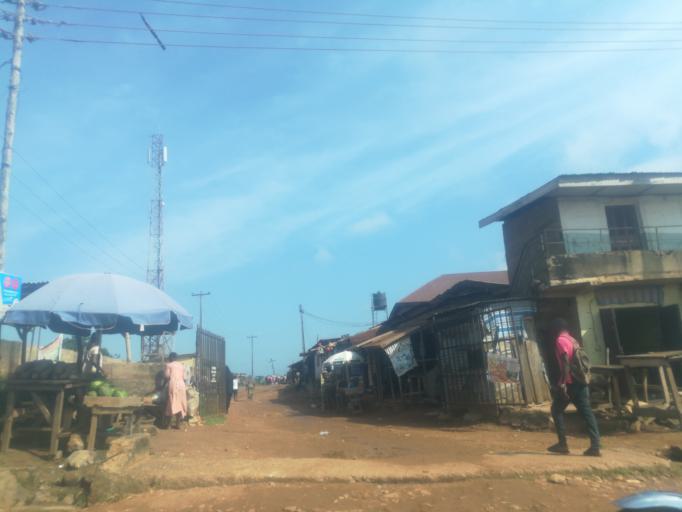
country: NG
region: Oyo
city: Ibadan
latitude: 7.3373
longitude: 3.8529
